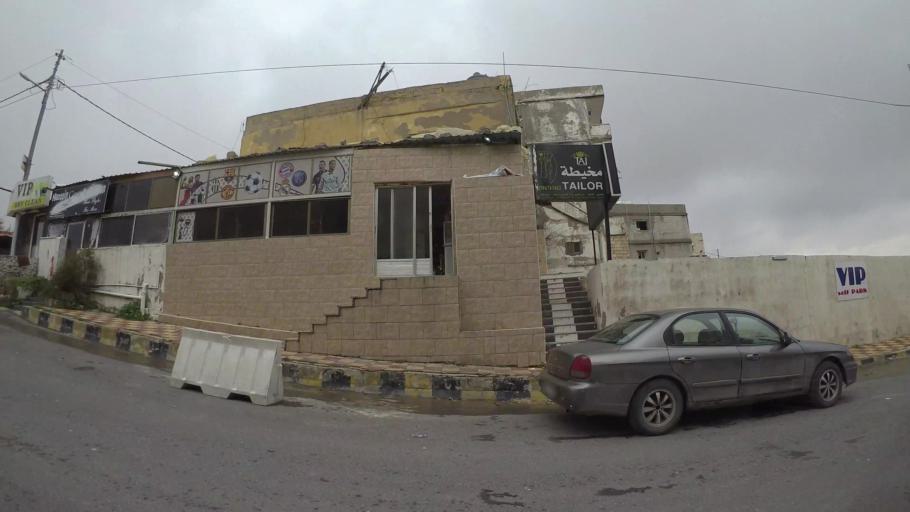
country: JO
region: Amman
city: Al Bunayyat ash Shamaliyah
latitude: 31.9421
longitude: 35.8876
